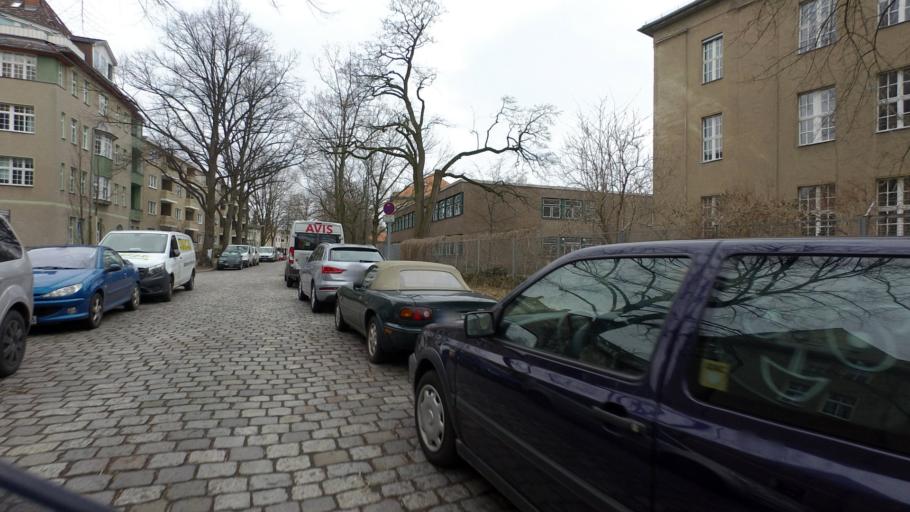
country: DE
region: Berlin
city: Marienfelde
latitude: 52.4279
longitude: 13.3571
